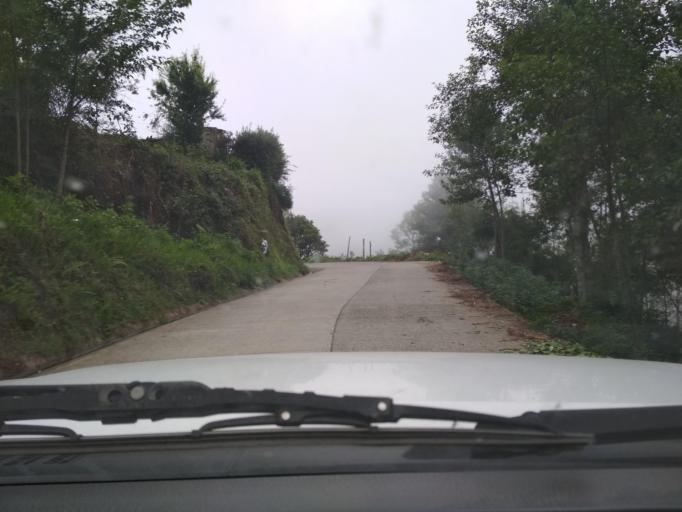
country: MX
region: Veracruz
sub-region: La Perla
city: Chilapa
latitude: 19.0002
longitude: -97.1615
